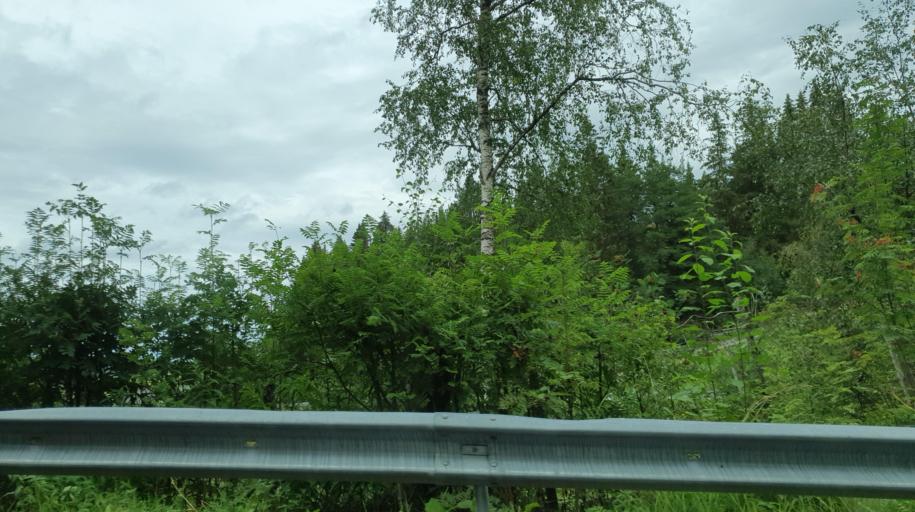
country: NO
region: Nord-Trondelag
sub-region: Stjordal
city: Stjordalshalsen
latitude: 63.4117
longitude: 10.9721
